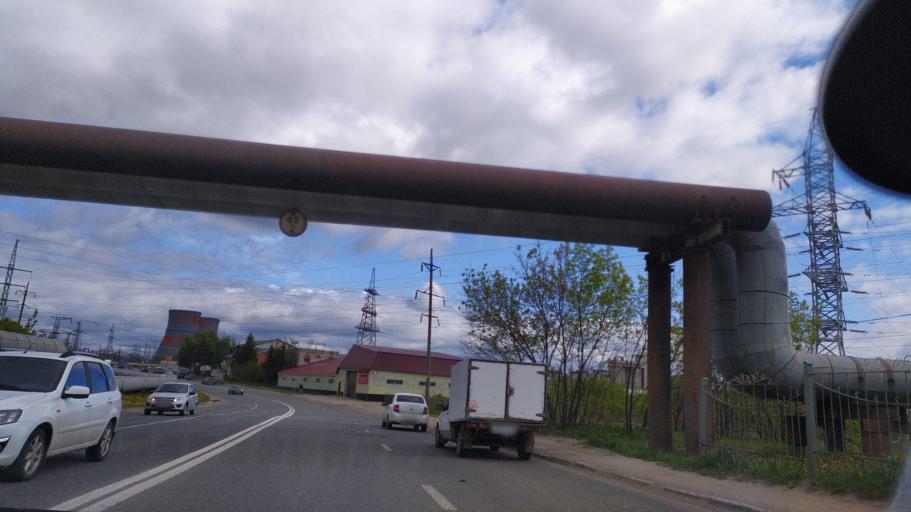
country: RU
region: Chuvashia
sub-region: Cheboksarskiy Rayon
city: Cheboksary
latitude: 56.1169
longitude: 47.3012
